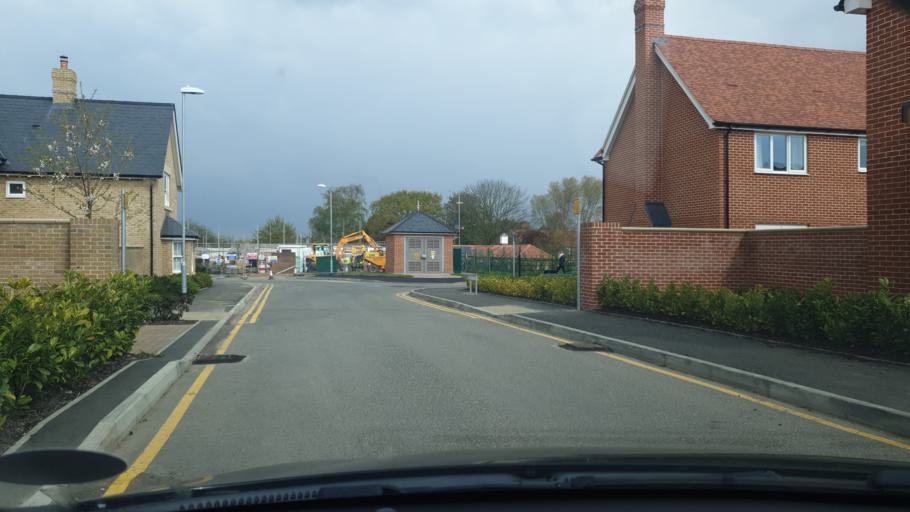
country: GB
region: England
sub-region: Essex
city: Manningtree
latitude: 51.9418
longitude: 1.0490
